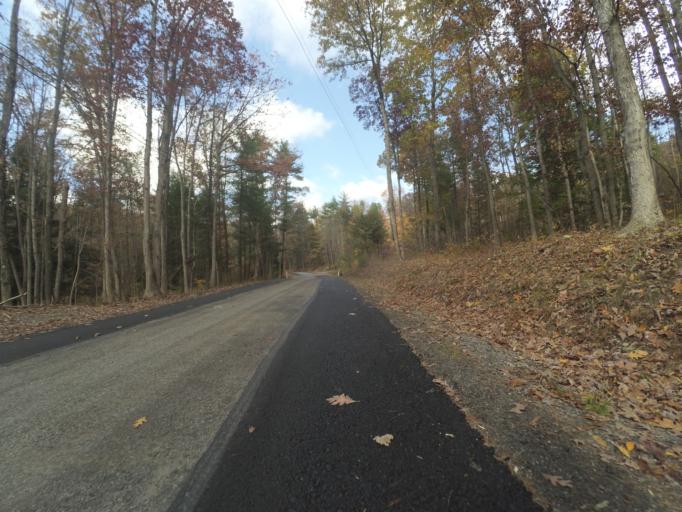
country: US
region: Pennsylvania
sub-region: Centre County
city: Stormstown
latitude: 40.8582
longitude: -77.9831
